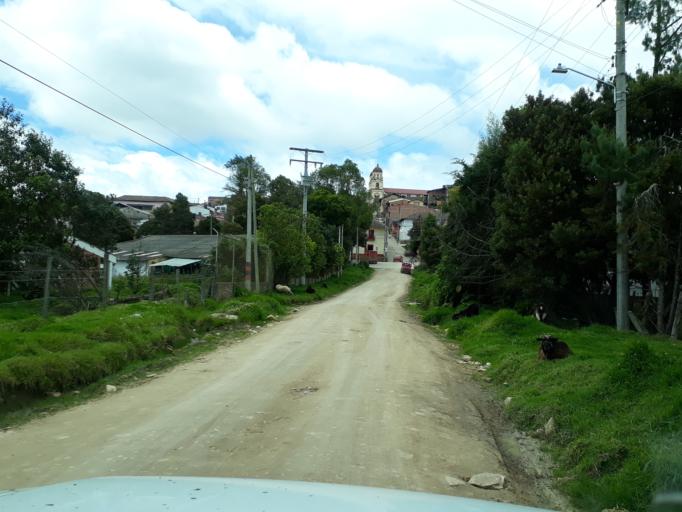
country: CO
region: Cundinamarca
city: Guasca
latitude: 4.8641
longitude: -73.8797
